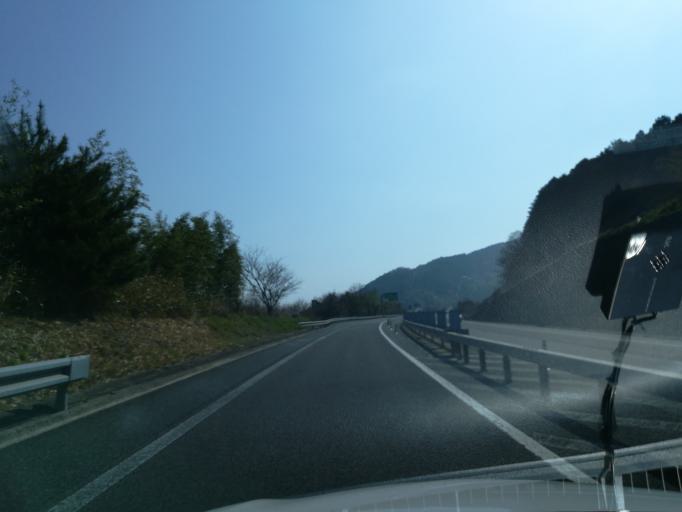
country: JP
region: Tokushima
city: Ikedacho
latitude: 34.0289
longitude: 133.8340
